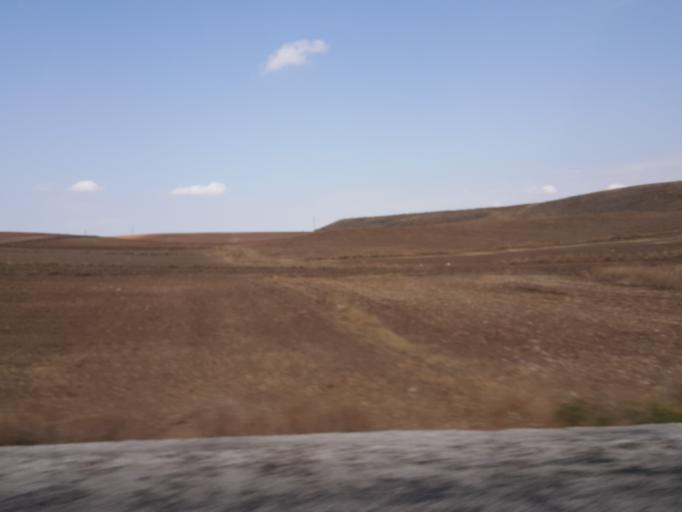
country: TR
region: Corum
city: Alaca
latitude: 40.1561
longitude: 34.7492
